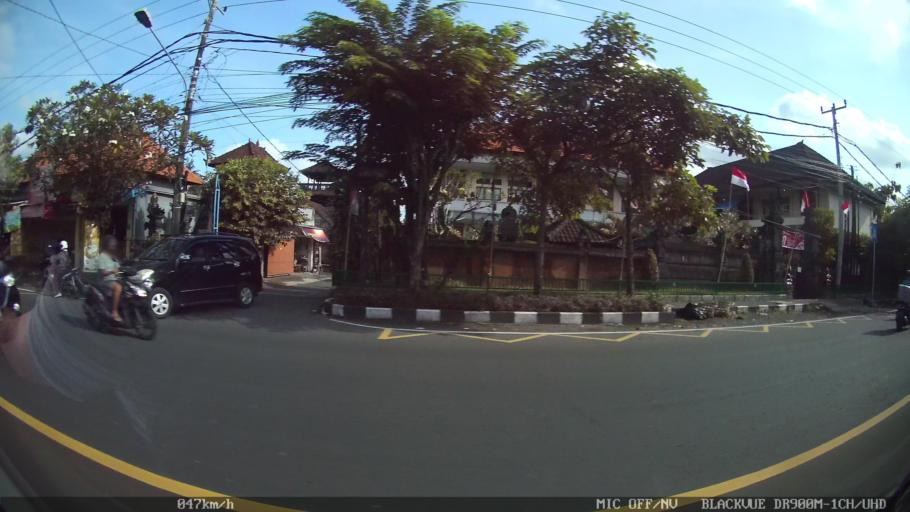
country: ID
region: Bali
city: Banjar Jumbayah
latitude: -8.5636
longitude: 115.1681
